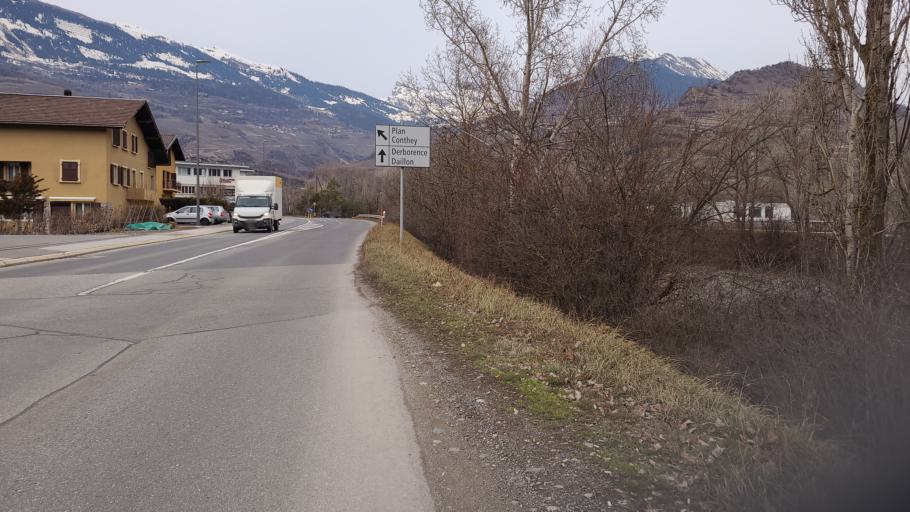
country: CH
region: Valais
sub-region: Conthey District
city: Conthey
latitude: 46.2284
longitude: 7.3126
